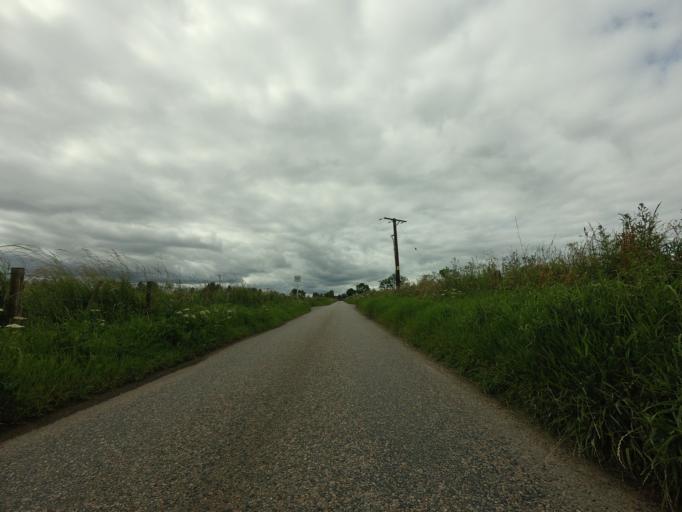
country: GB
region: Scotland
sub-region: Moray
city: Forres
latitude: 57.6181
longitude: -3.6176
